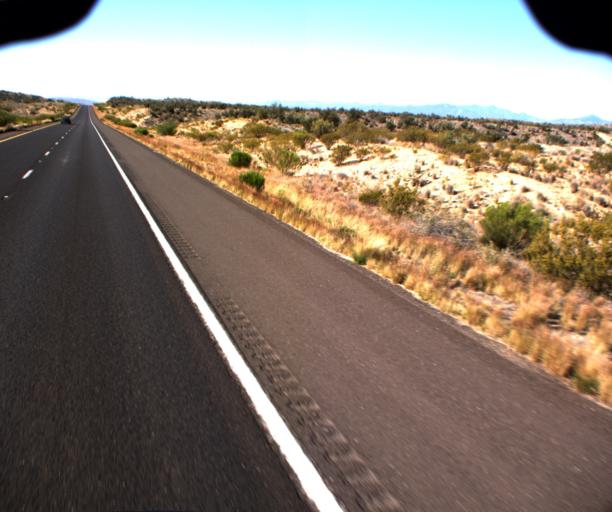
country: US
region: Arizona
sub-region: Mohave County
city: Kingman
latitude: 35.0972
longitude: -113.6664
